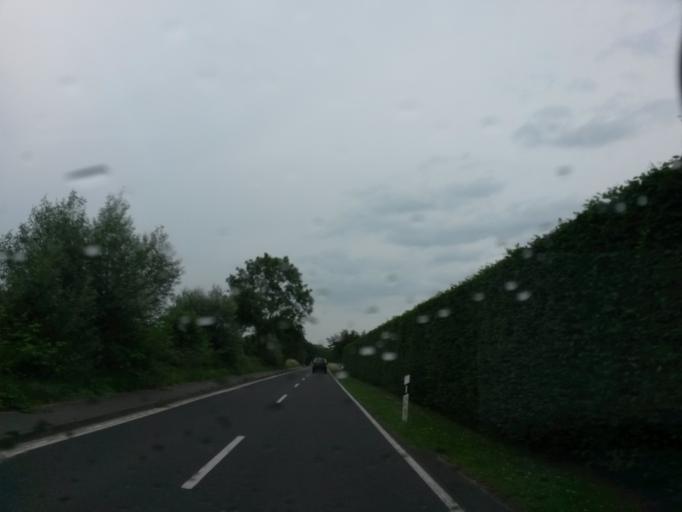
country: DE
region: North Rhine-Westphalia
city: Lohmar
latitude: 50.8502
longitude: 7.2449
